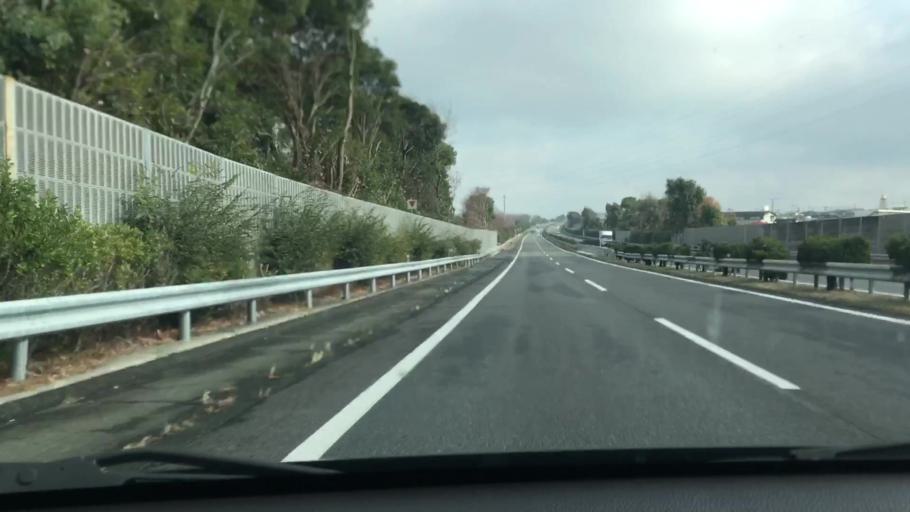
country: JP
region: Kumamoto
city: Ueki
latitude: 32.8587
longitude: 130.7491
